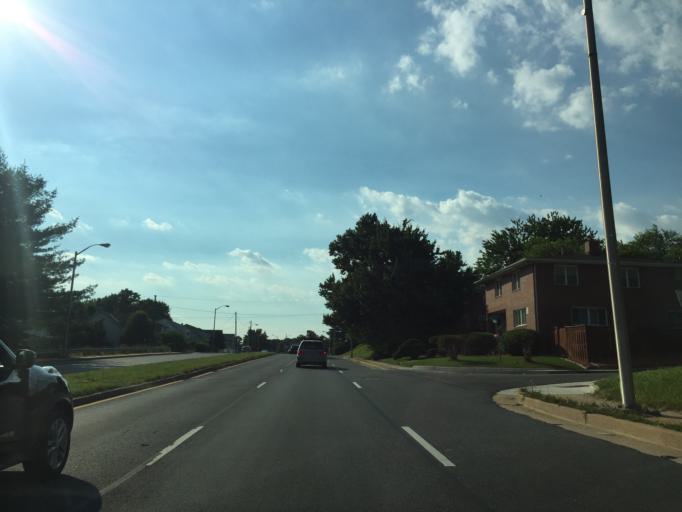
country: US
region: Maryland
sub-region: Baltimore County
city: Rosedale
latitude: 39.3294
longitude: -76.5592
